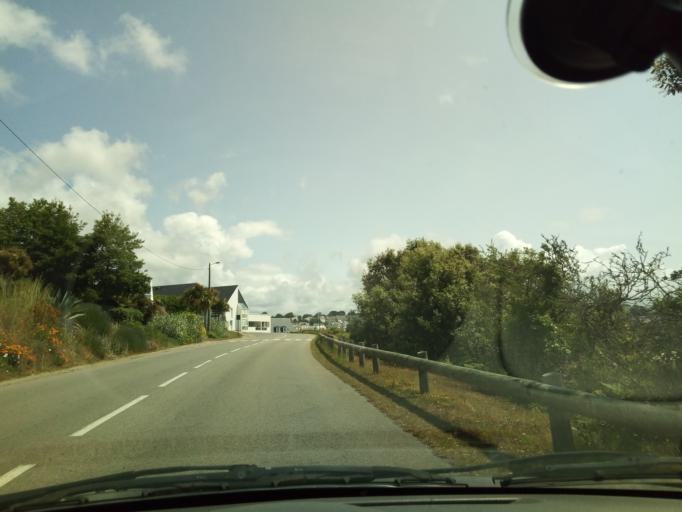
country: FR
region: Brittany
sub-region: Departement du Finistere
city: Audierne
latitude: 48.0176
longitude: -4.5377
